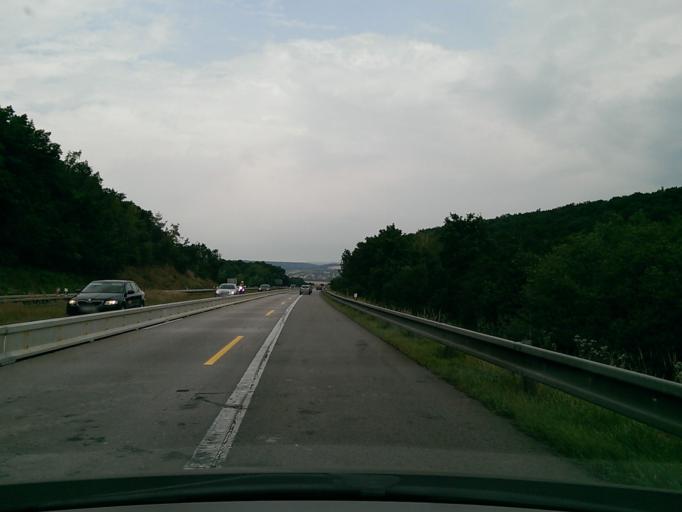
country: CZ
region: South Moravian
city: Ricany
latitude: 49.1946
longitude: 16.4320
